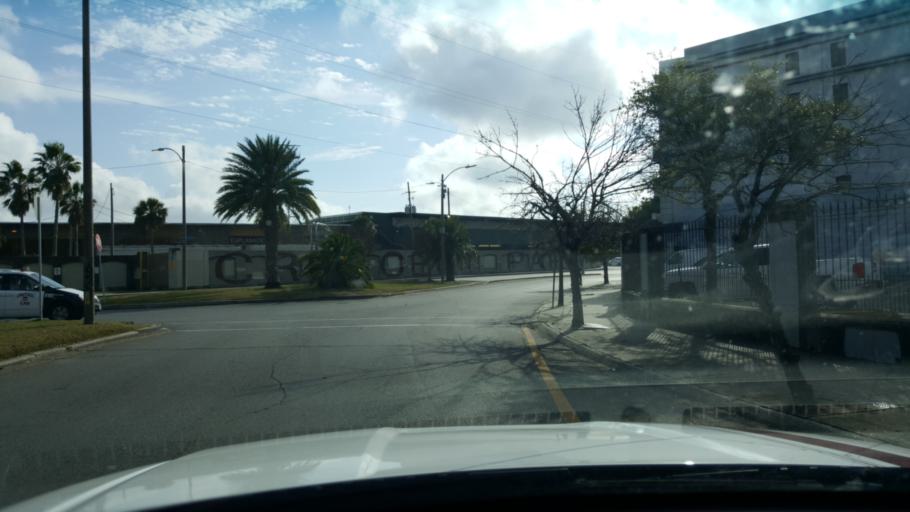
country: US
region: Louisiana
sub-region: Orleans Parish
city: New Orleans
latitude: 29.9622
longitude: -90.0565
